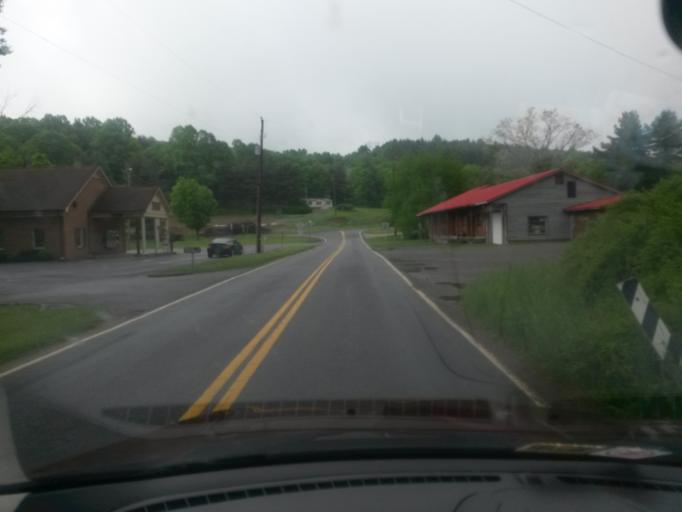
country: US
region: Virginia
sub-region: Patrick County
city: Stuart
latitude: 36.7391
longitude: -80.3900
